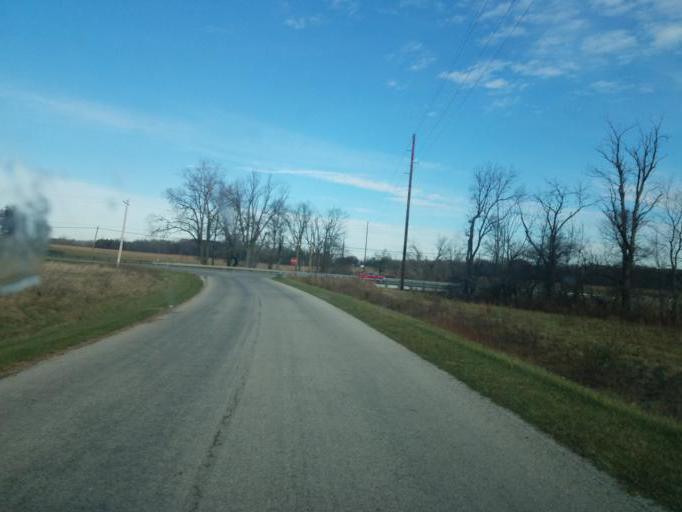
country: US
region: Ohio
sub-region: Crawford County
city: Galion
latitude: 40.7325
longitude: -82.7458
